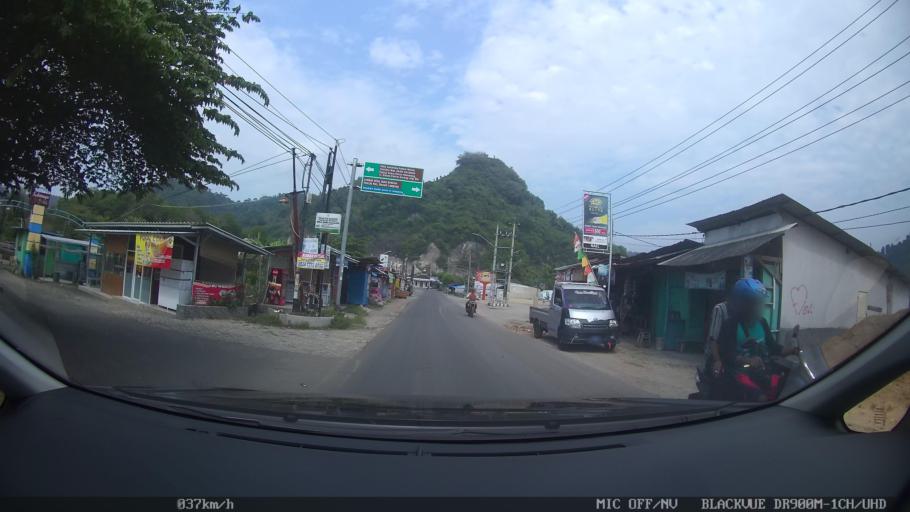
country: ID
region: Lampung
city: Bandarlampung
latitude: -5.4643
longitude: 105.2455
